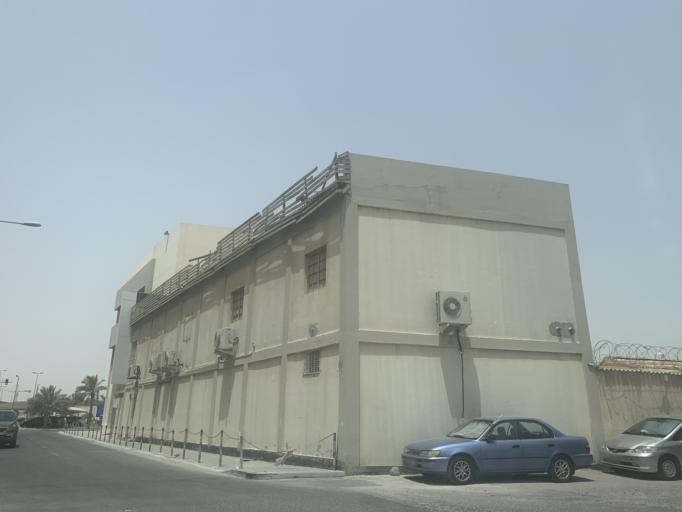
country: BH
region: Manama
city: Jidd Hafs
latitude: 26.2077
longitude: 50.5414
